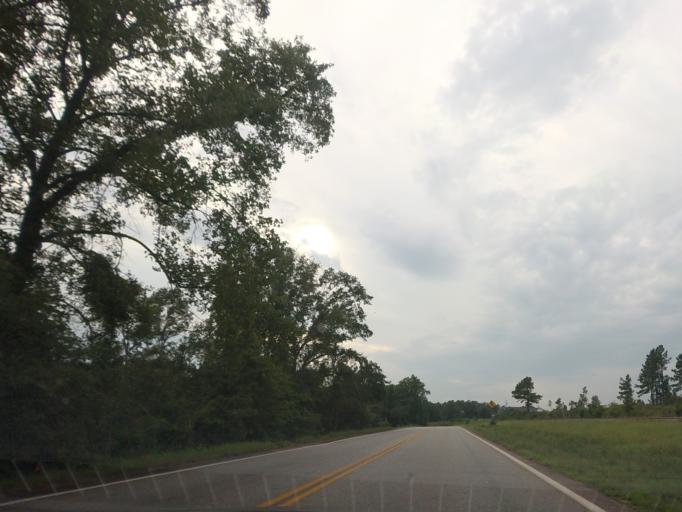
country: US
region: Georgia
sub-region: Twiggs County
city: Jeffersonville
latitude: 32.7182
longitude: -83.3982
